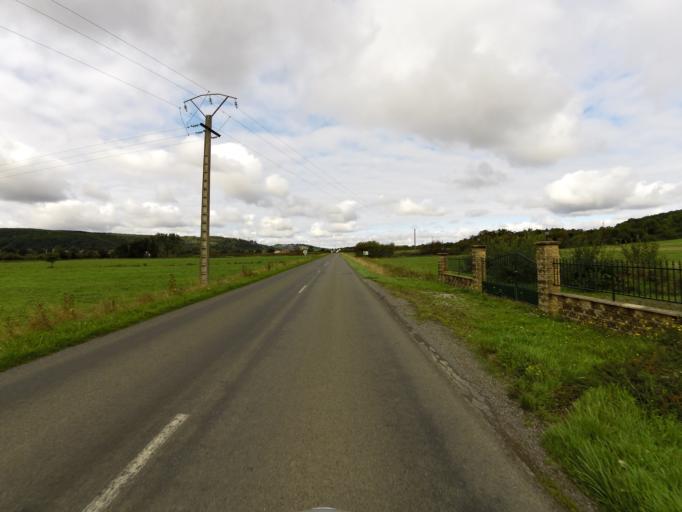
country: FR
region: Champagne-Ardenne
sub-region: Departement des Ardennes
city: Fromelennes
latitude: 50.1321
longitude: 4.8642
